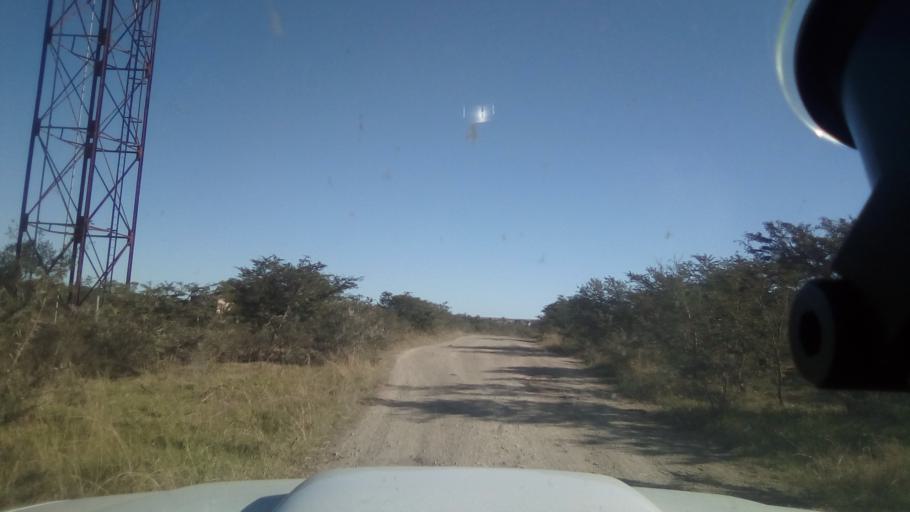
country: ZA
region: Eastern Cape
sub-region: Buffalo City Metropolitan Municipality
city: Bhisho
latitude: -32.7551
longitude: 27.3350
